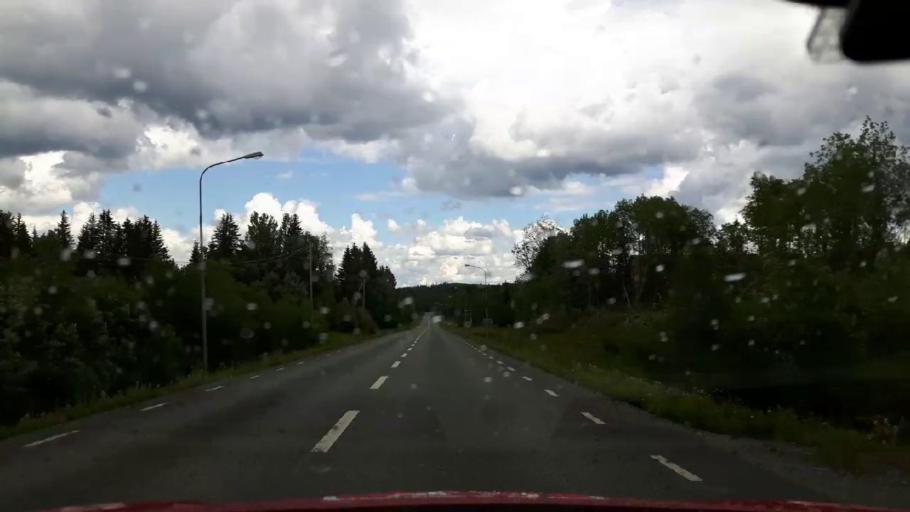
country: SE
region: Jaemtland
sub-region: Krokoms Kommun
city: Krokom
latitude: 63.7615
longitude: 14.3158
